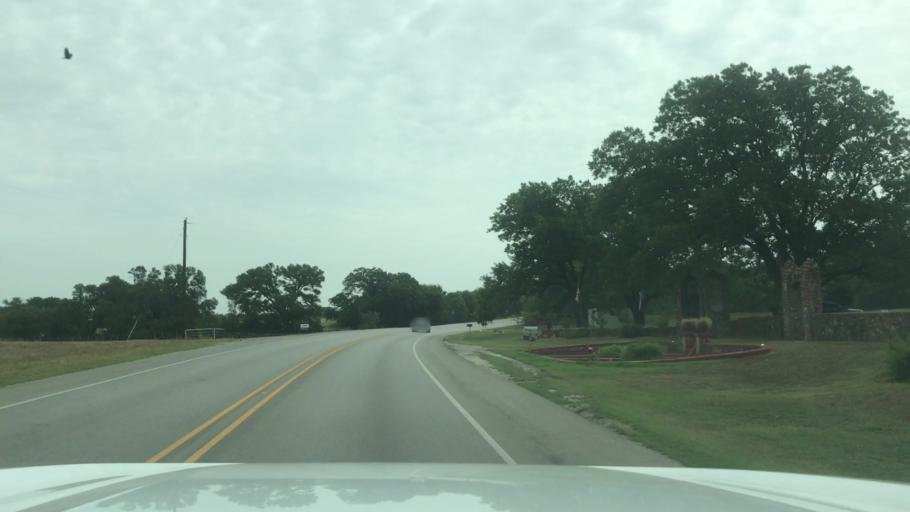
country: US
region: Texas
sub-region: Erath County
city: Dublin
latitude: 32.0984
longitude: -98.3989
